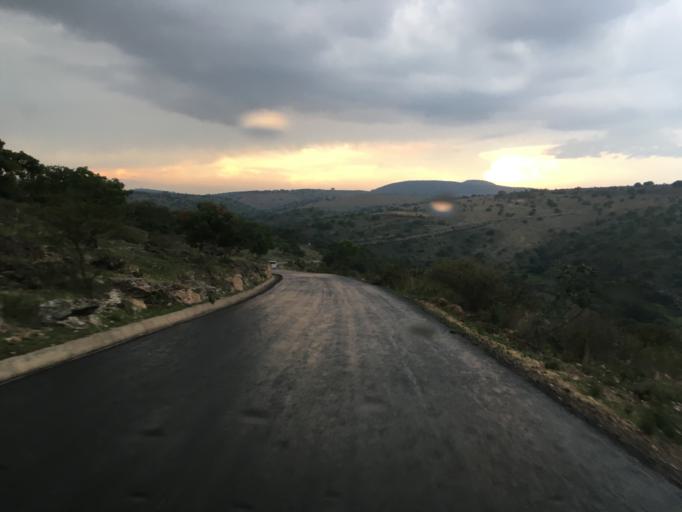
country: MX
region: Oaxaca
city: Santiago Tilantongo
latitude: 17.2902
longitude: -97.2769
